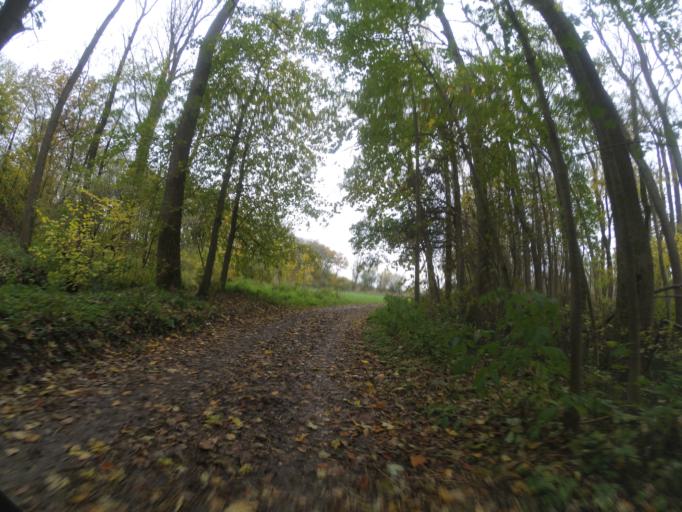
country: DE
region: Baden-Wuerttemberg
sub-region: Tuebingen Region
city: Staig
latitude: 48.3466
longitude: 9.9987
